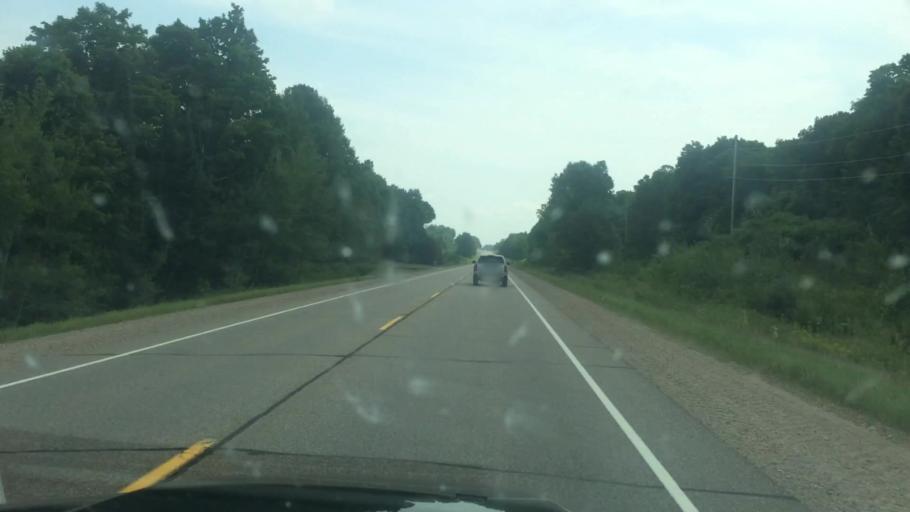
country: US
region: Wisconsin
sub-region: Langlade County
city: Antigo
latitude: 45.1615
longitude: -89.0491
